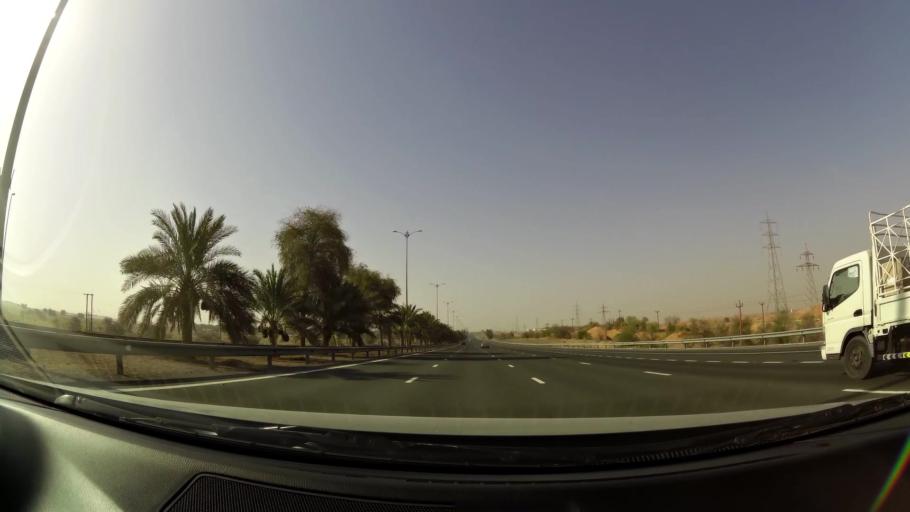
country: OM
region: Al Buraimi
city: Al Buraymi
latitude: 24.4701
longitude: 55.7779
